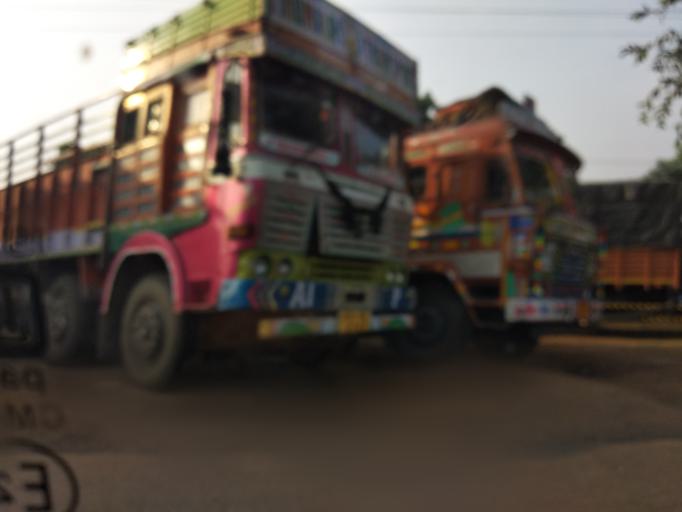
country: IN
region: Andhra Pradesh
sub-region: Vishakhapatnam
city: Visakhapatnam
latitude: 17.6847
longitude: 83.1582
